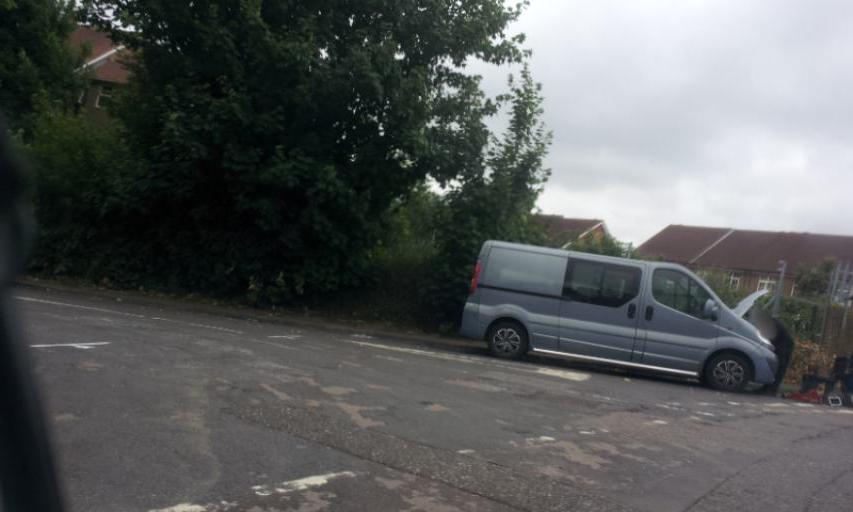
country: GB
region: England
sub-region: Kent
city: Sittingbourne
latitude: 51.3437
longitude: 0.7281
